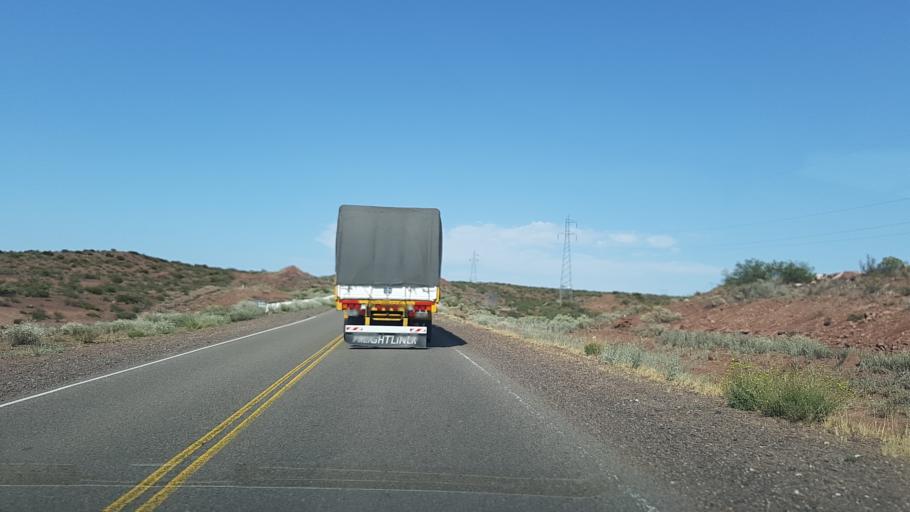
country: AR
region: Neuquen
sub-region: Departamento de Picun Leufu
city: Picun Leufu
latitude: -39.3006
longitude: -68.9177
